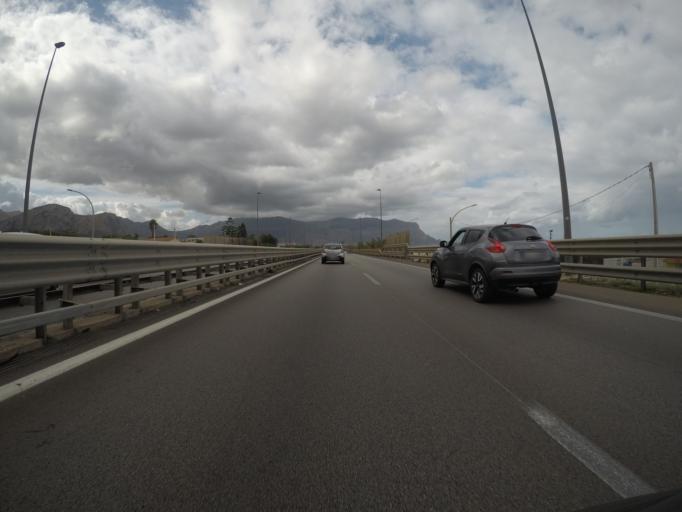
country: IT
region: Sicily
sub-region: Palermo
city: Capaci
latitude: 38.1804
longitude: 13.2314
